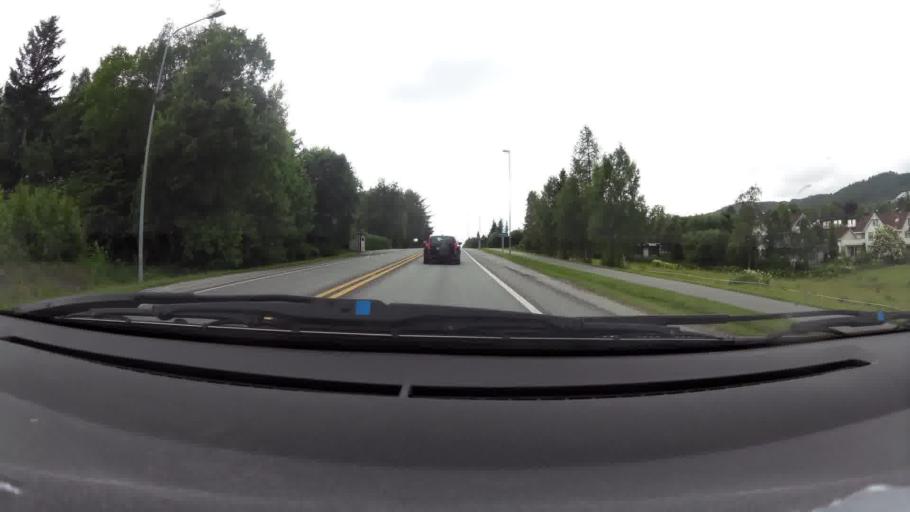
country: NO
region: More og Romsdal
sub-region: Molde
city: Molde
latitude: 62.7441
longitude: 7.2404
